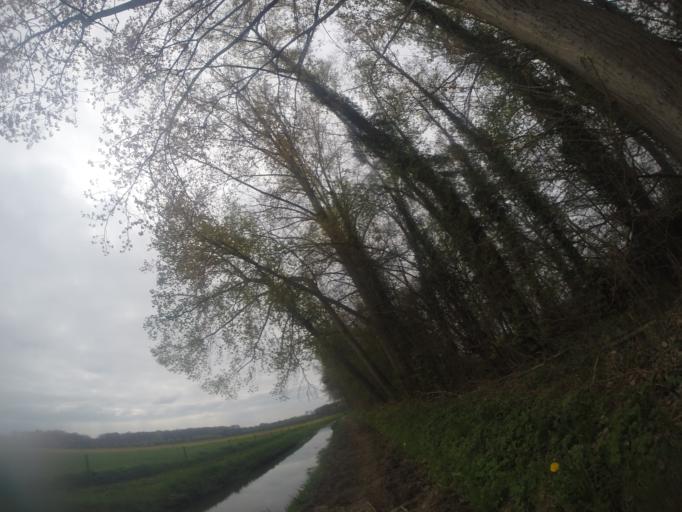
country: NL
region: Gelderland
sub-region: Gemeente Zutphen
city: Leesten
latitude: 52.1163
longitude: 6.2740
